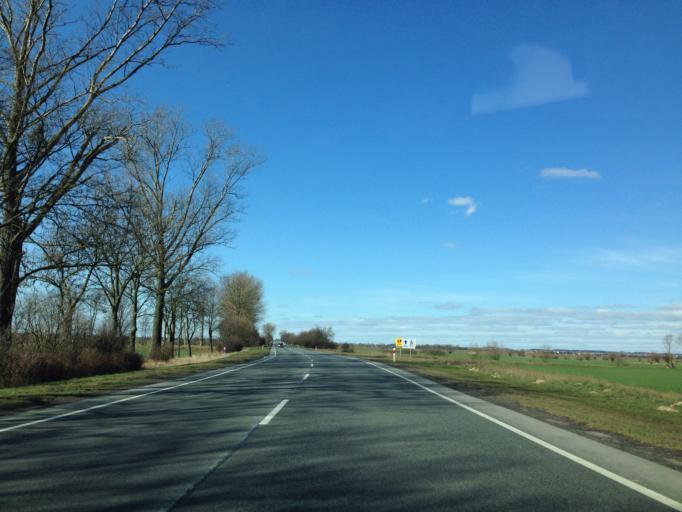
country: PL
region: Pomeranian Voivodeship
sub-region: Powiat malborski
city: Lisewo Malborskie
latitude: 54.0547
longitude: 18.8485
